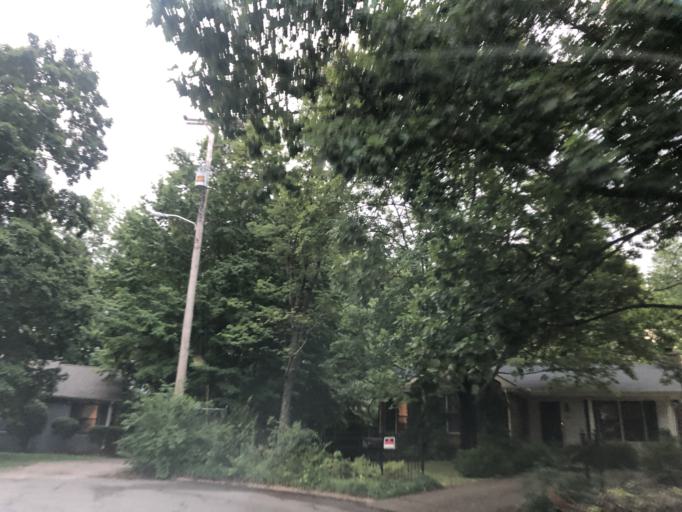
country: US
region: Tennessee
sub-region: Davidson County
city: Lakewood
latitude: 36.1468
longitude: -86.6292
